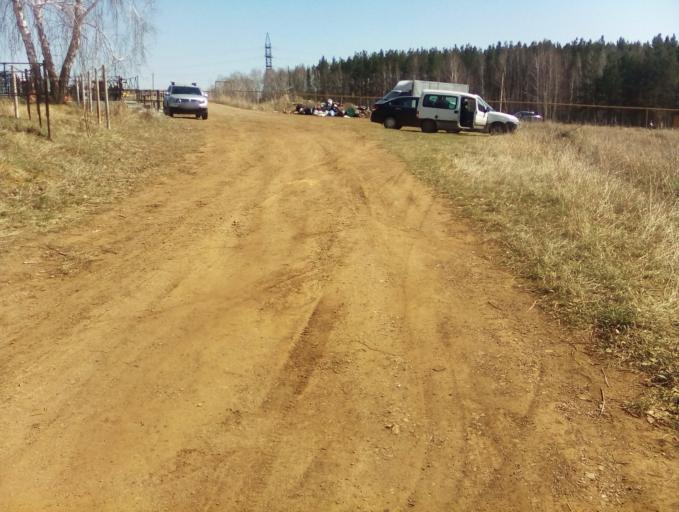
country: RU
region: Chelyabinsk
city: Sargazy
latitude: 55.0325
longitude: 61.2403
